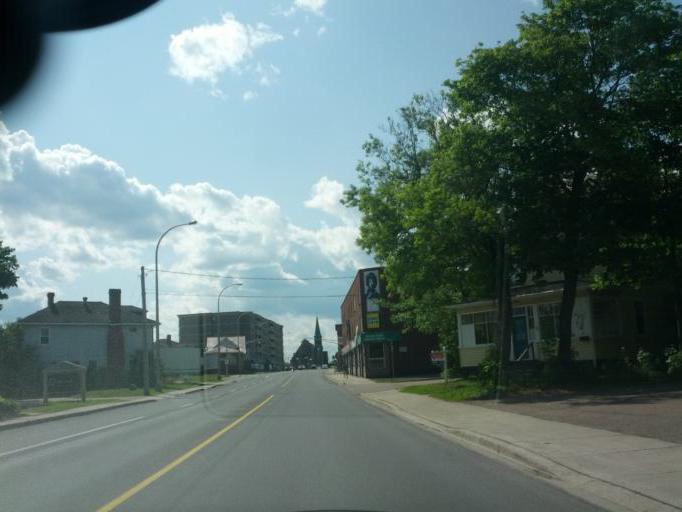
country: CA
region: New Brunswick
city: Moncton
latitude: 46.0960
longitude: -64.7905
